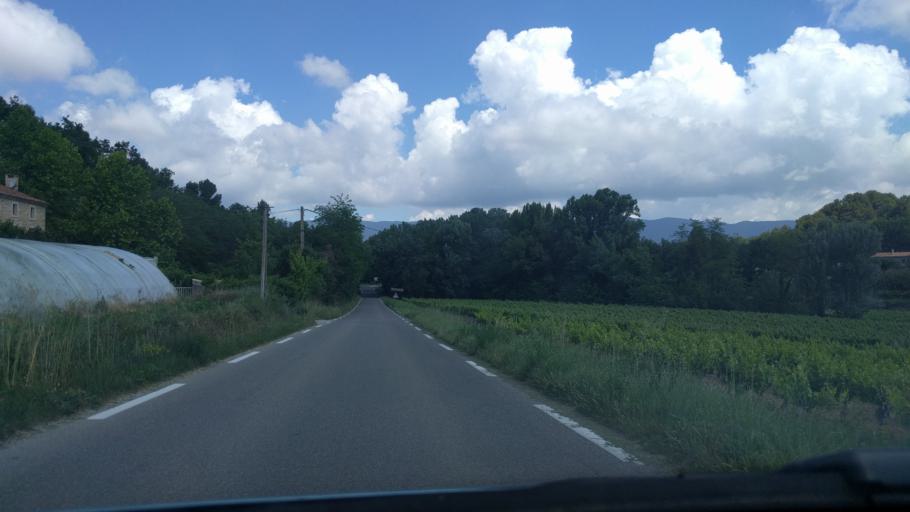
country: FR
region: Provence-Alpes-Cote d'Azur
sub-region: Departement du Vaucluse
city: Pertuis
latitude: 43.7441
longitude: 5.5259
